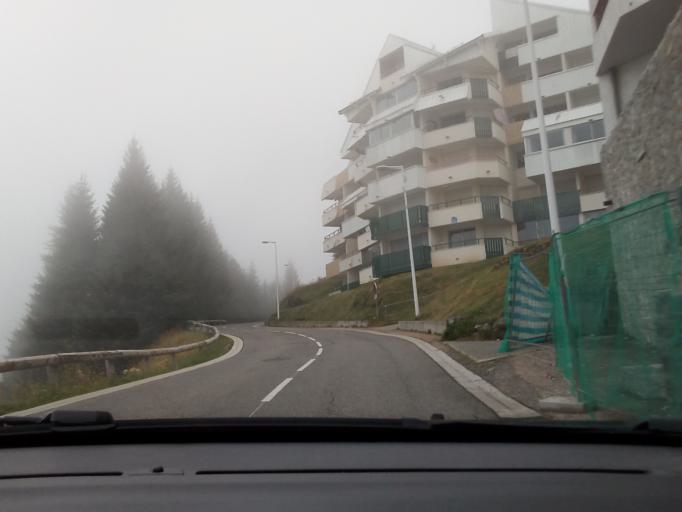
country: FR
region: Aquitaine
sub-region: Departement des Pyrenees-Atlantiques
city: Laruns
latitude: 42.9589
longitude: -0.3327
